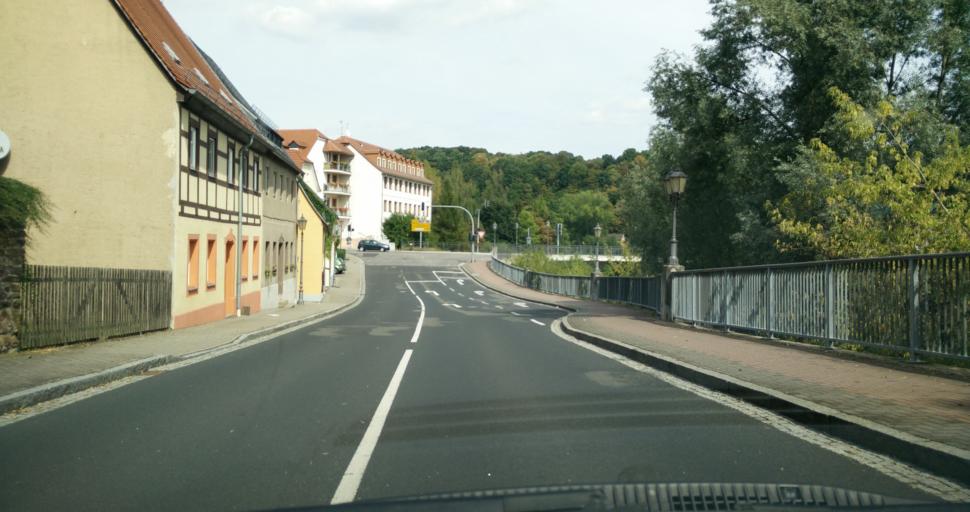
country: DE
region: Saxony
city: Colditz
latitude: 51.1303
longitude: 12.8015
